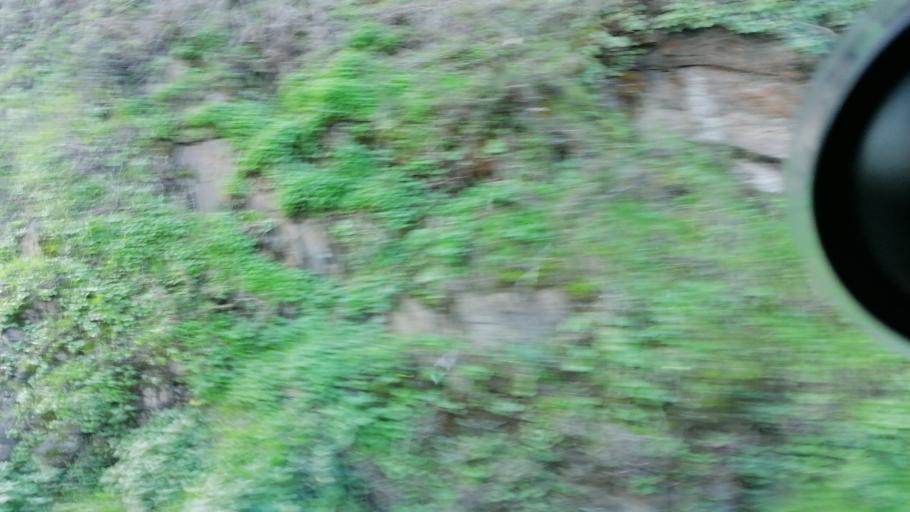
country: PT
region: Vila Real
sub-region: Peso da Regua
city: Peso da Regua
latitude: 41.1394
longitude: -7.7776
